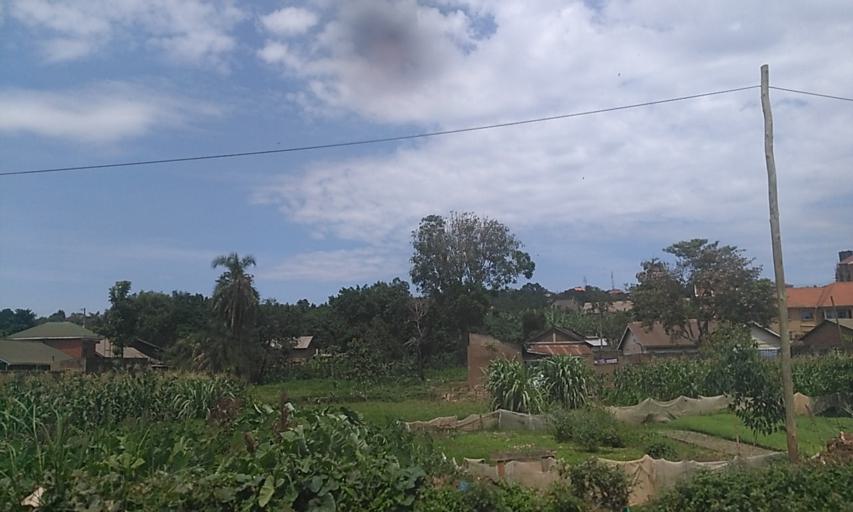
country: UG
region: Central Region
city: Kampala Central Division
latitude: 0.3521
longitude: 32.5765
